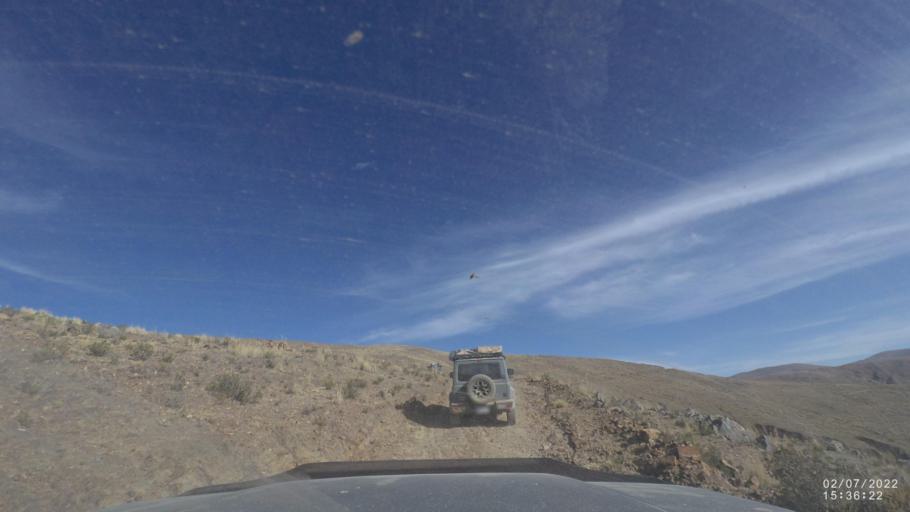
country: BO
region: Cochabamba
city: Irpa Irpa
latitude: -17.8901
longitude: -66.4105
